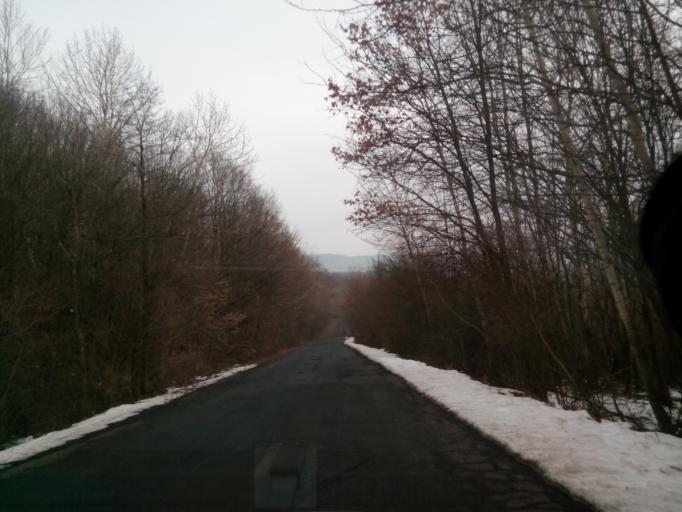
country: HU
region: Borsod-Abauj-Zemplen
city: Gonc
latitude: 48.4848
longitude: 21.3953
